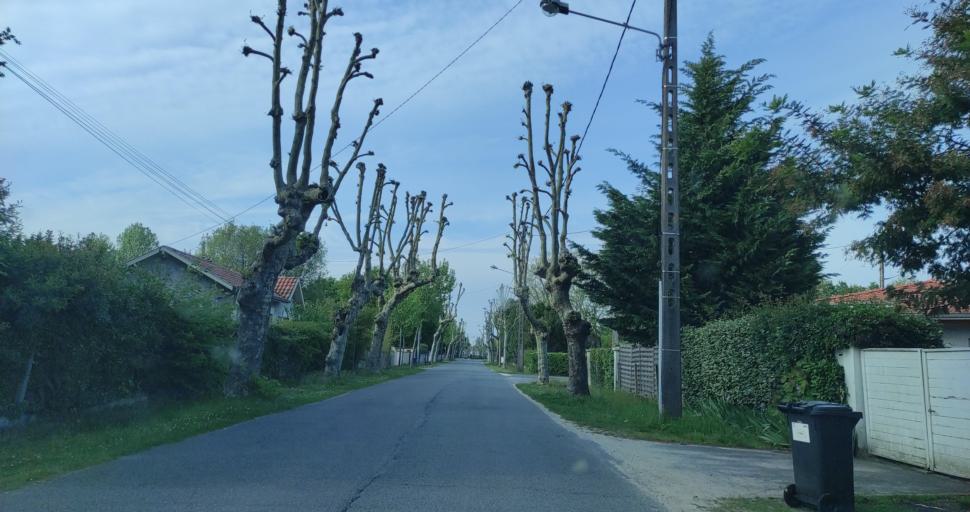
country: FR
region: Aquitaine
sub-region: Departement de la Gironde
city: Ares
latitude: 44.7588
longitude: -1.1330
